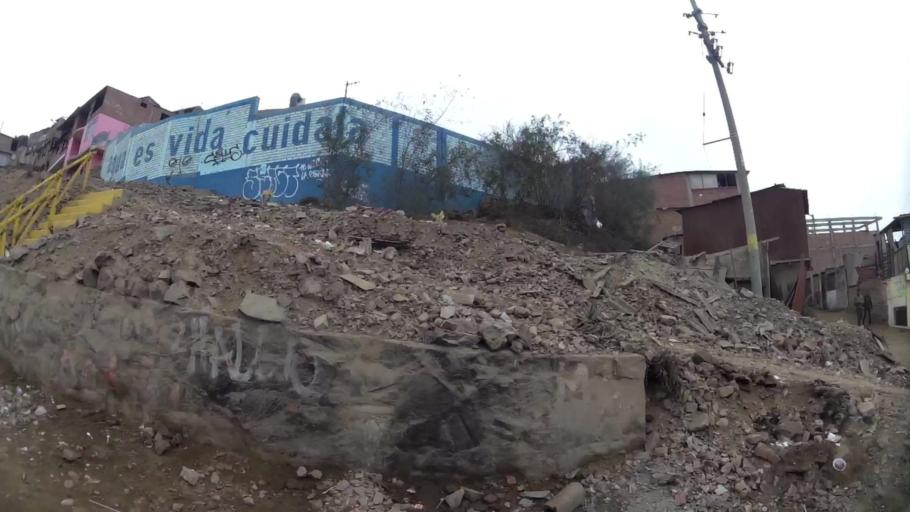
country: PE
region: Lima
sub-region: Lima
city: Surco
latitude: -12.1671
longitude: -76.9563
